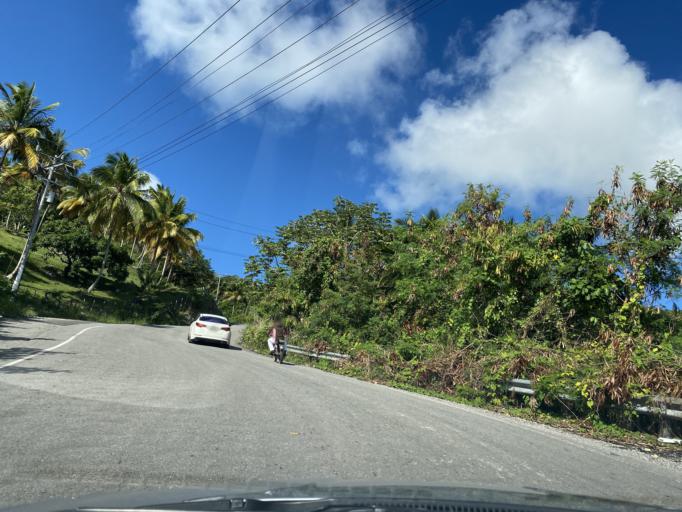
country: DO
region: Samana
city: Sanchez
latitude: 19.2355
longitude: -69.5960
